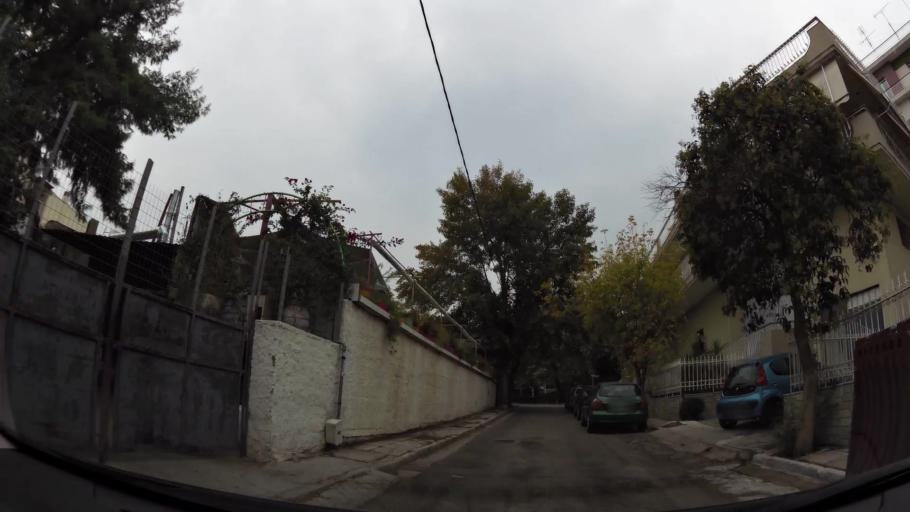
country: GR
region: Attica
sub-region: Nomarchia Athinas
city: Chaidari
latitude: 38.0023
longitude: 23.6639
